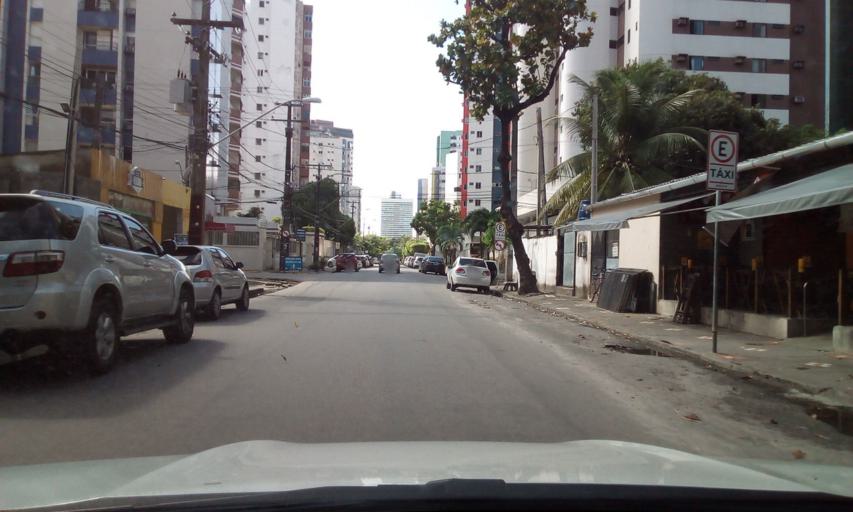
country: BR
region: Pernambuco
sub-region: Recife
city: Recife
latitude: -8.1264
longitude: -34.9037
